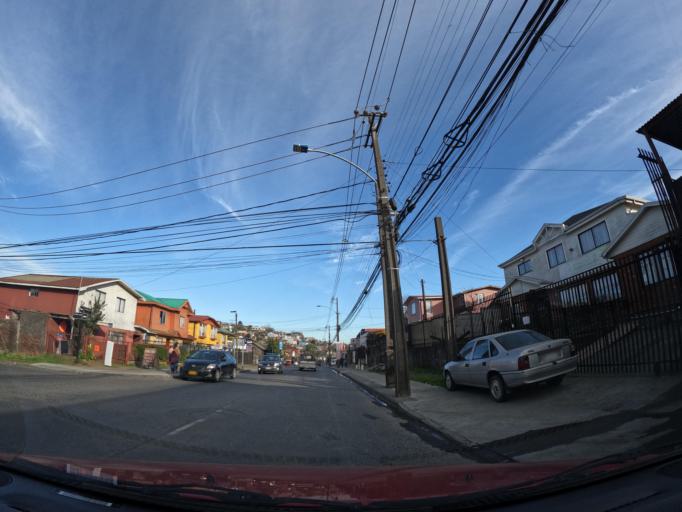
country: CL
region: Biobio
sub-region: Provincia de Concepcion
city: Concepcion
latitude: -36.7922
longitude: -73.0457
